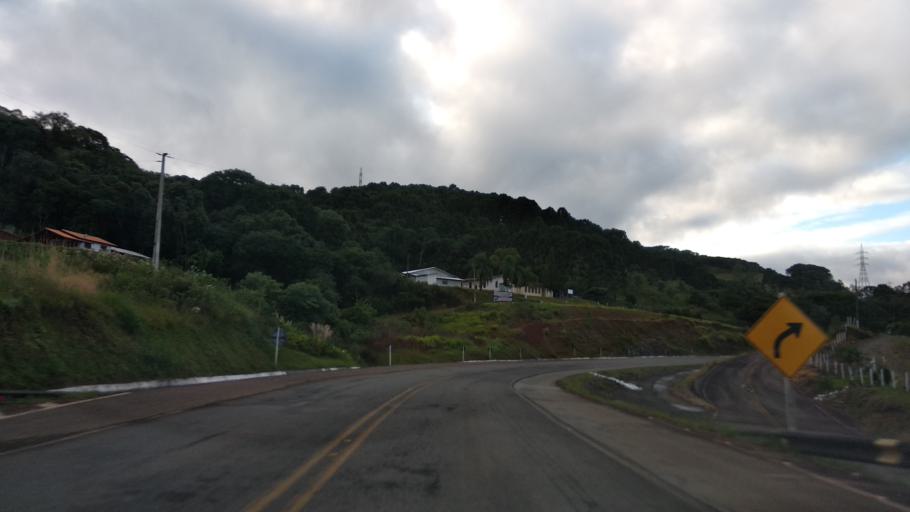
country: BR
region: Santa Catarina
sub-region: Curitibanos
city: Curitibanos
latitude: -27.5382
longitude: -50.8595
